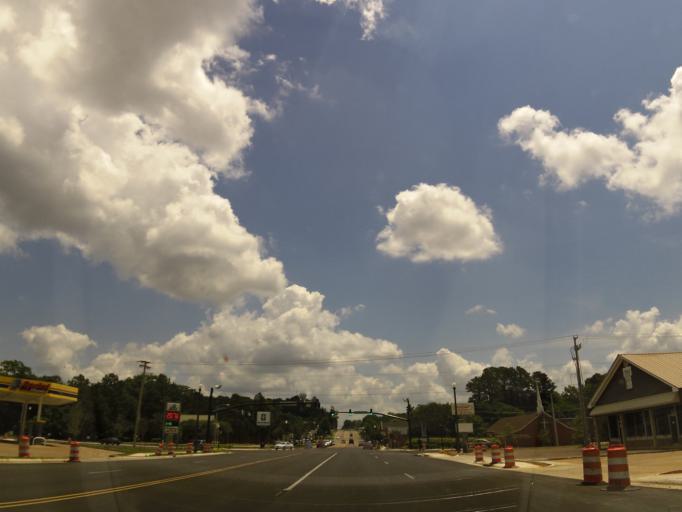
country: US
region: Mississippi
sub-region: Lee County
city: Tupelo
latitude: 34.2575
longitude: -88.6842
